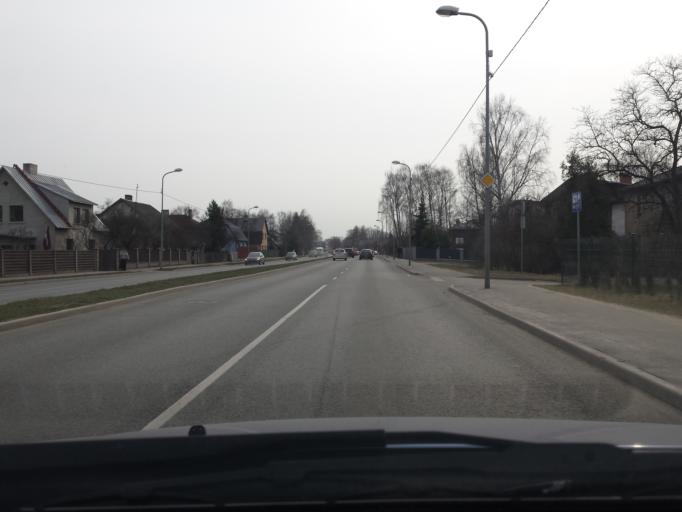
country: LV
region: Riga
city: Riga
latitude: 56.9475
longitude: 24.1841
